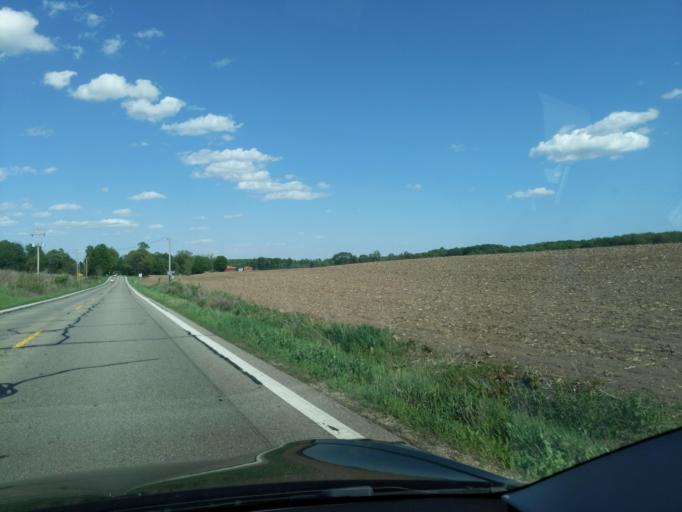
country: US
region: Michigan
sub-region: Kent County
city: Lowell
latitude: 42.7985
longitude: -85.3485
